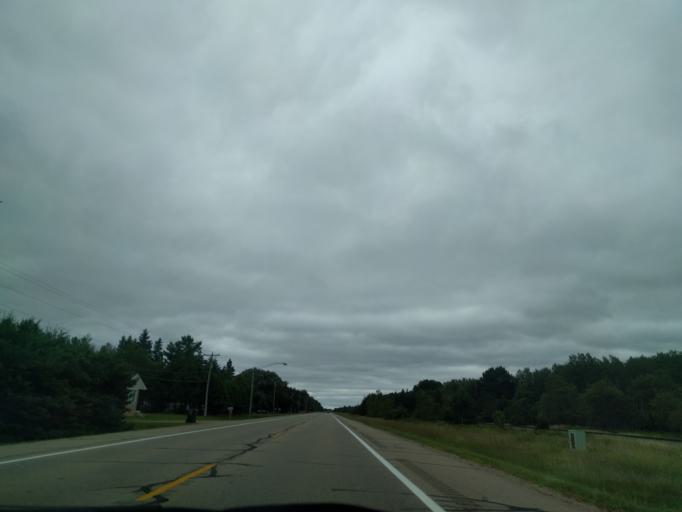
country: US
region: Michigan
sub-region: Delta County
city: Gladstone
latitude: 45.8804
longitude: -87.0648
